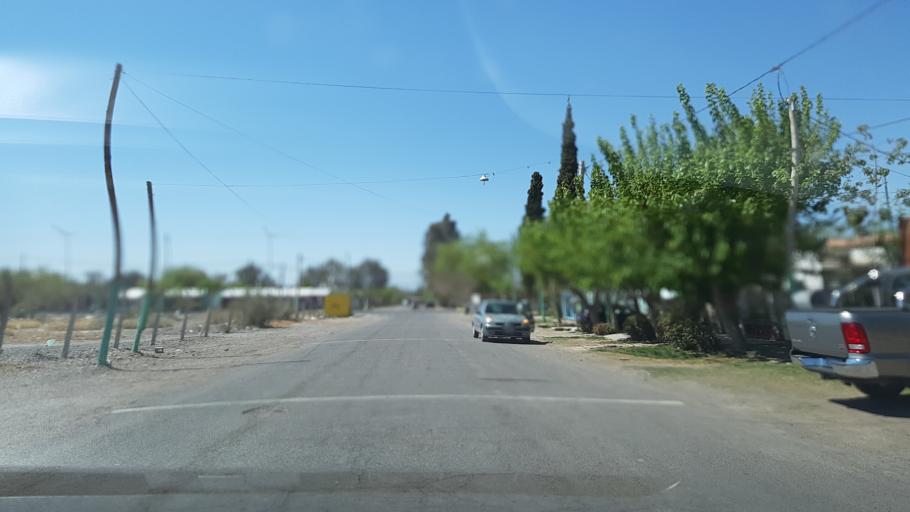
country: AR
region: San Juan
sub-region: Departamento de Rivadavia
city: Rivadavia
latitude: -31.5242
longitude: -68.6287
